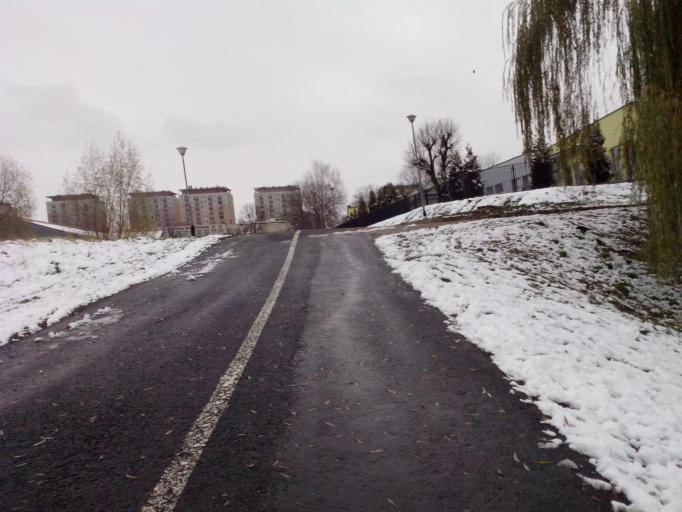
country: PL
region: Subcarpathian Voivodeship
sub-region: Rzeszow
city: Rzeszow
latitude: 50.0237
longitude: 21.9981
